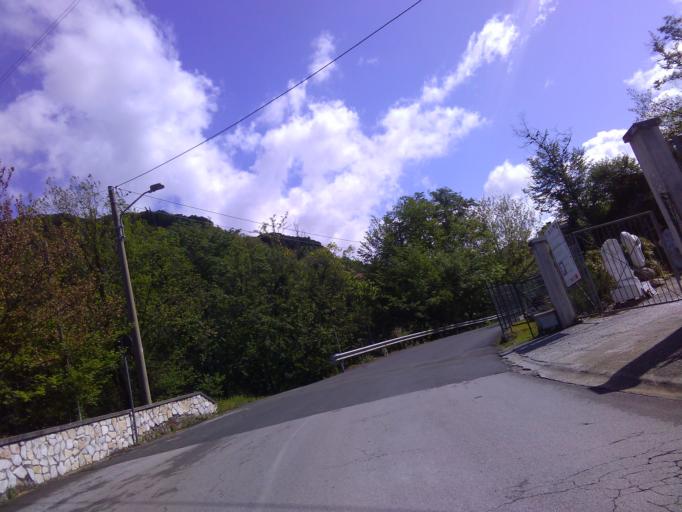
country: IT
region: Tuscany
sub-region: Provincia di Massa-Carrara
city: Carrara
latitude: 44.0788
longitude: 10.1092
